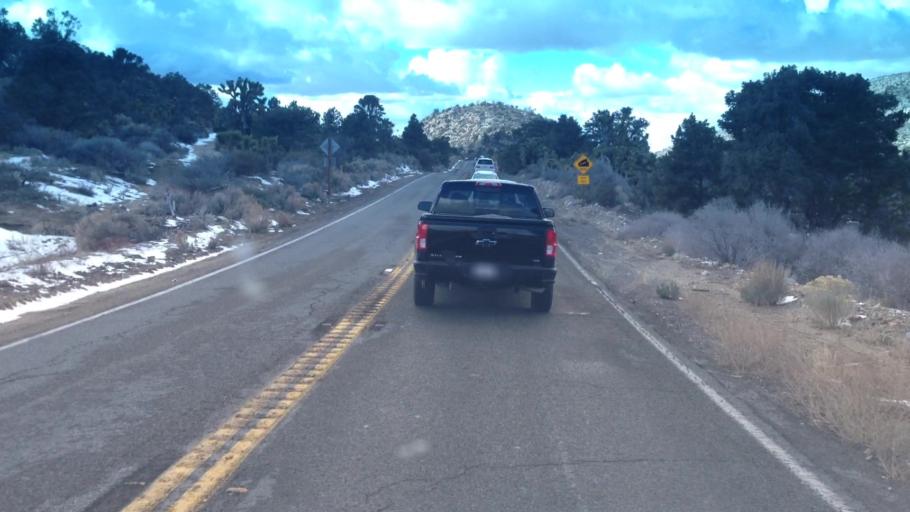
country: US
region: California
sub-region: San Bernardino County
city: Big Bear City
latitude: 34.3223
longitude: -116.8186
